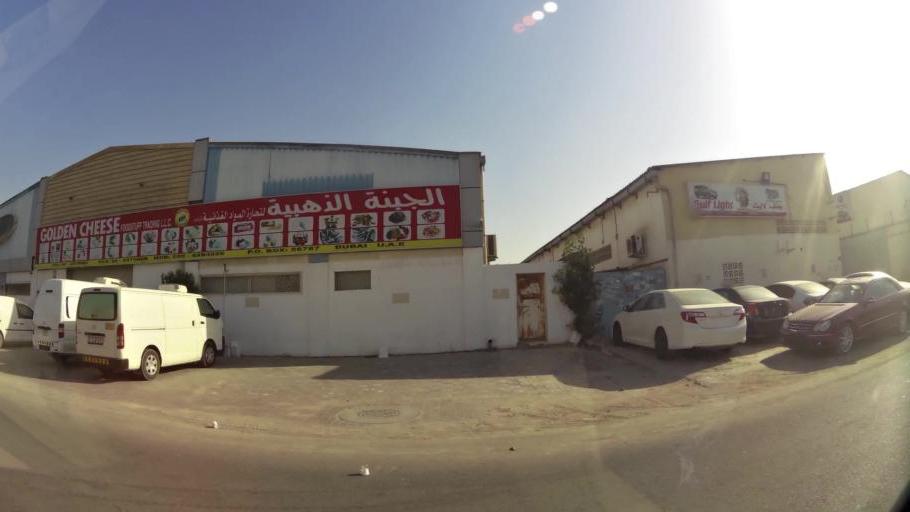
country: AE
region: Ash Shariqah
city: Sharjah
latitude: 25.2916
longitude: 55.3883
